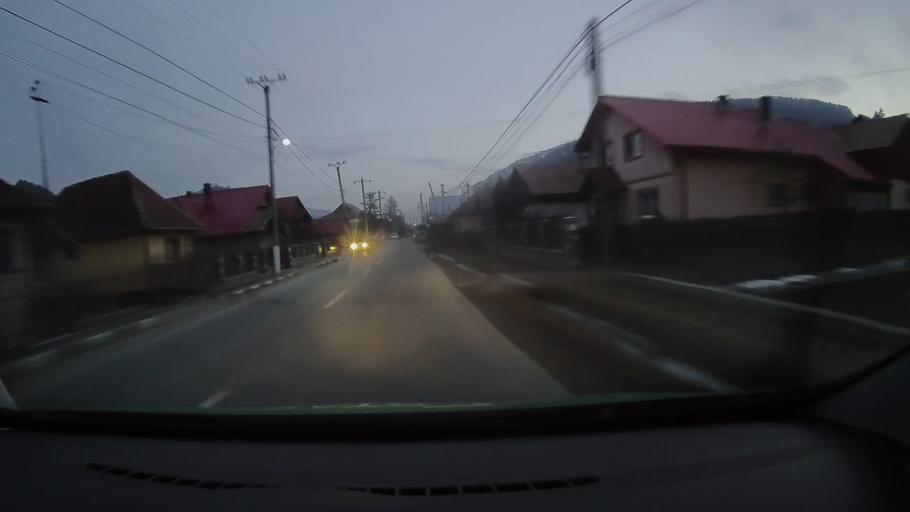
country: RO
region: Prahova
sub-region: Comuna Valea Doftanei
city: Tesila
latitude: 45.2920
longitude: 25.7222
